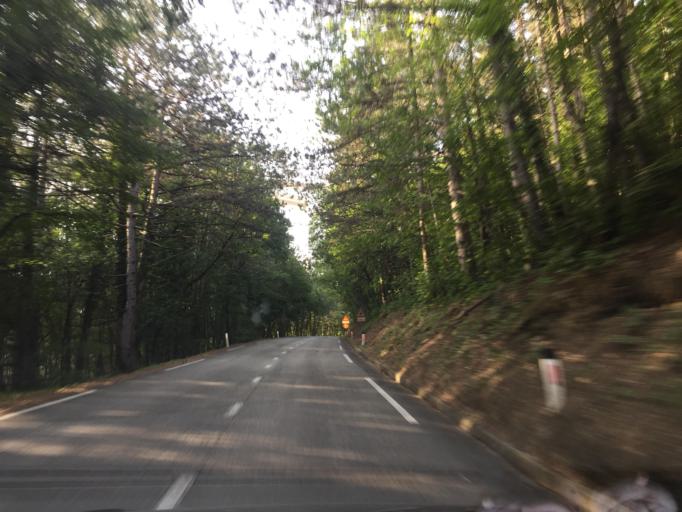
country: IT
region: Friuli Venezia Giulia
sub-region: Provincia di Trieste
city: Dolina
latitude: 45.5570
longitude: 13.8667
